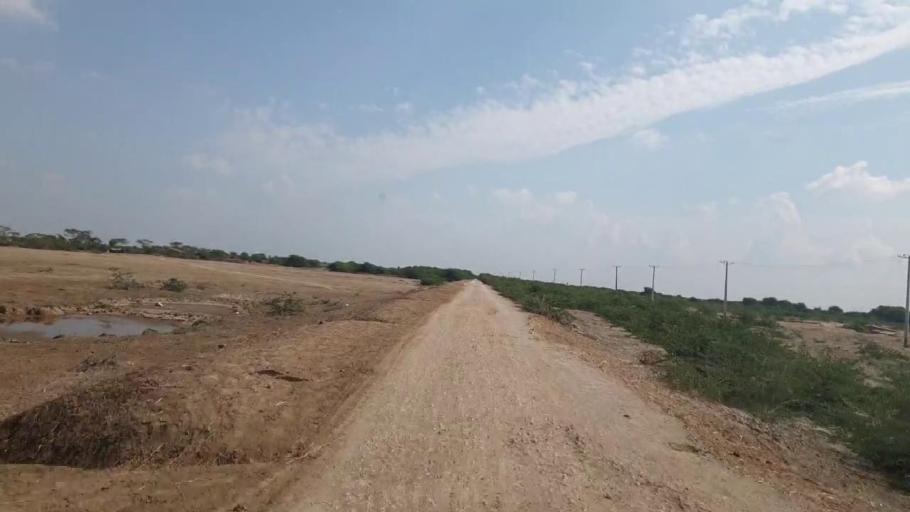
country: PK
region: Sindh
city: Badin
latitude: 24.4783
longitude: 68.6171
